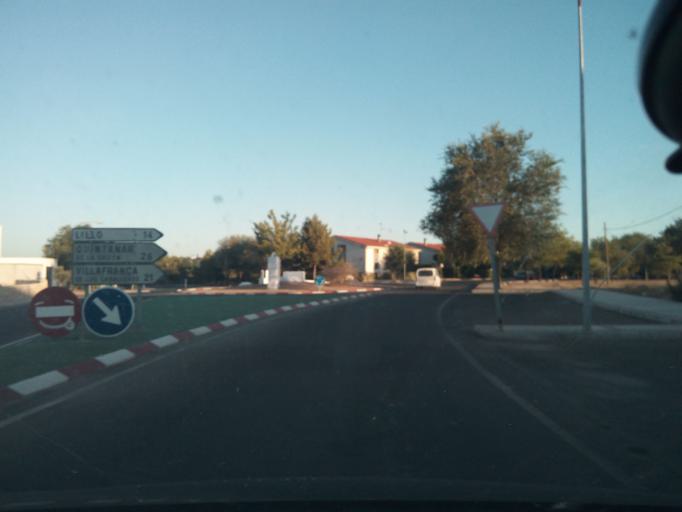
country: ES
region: Castille-La Mancha
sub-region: Province of Toledo
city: Villacanas
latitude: 39.6142
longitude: -3.3368
